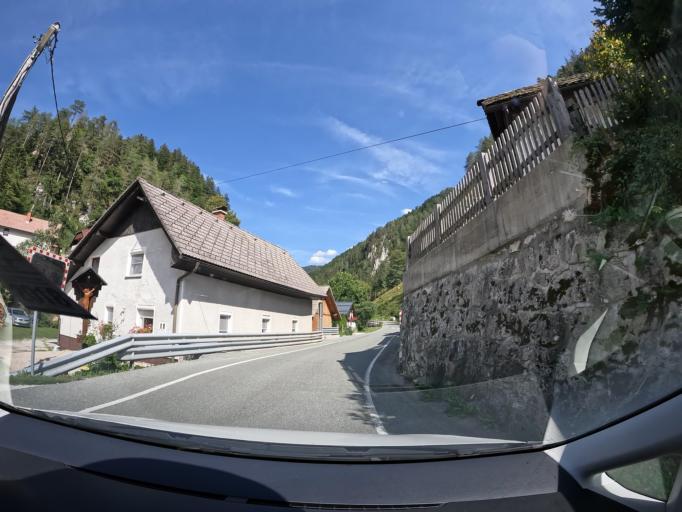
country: SI
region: Jesenice
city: Koroska Bela
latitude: 46.4650
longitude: 14.0948
